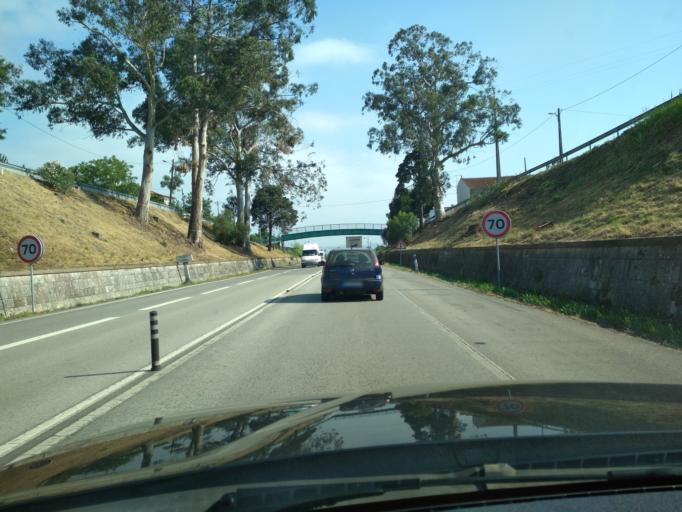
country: PT
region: Aveiro
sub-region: Mealhada
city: Pampilhosa do Botao
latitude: 40.2909
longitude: -8.4462
